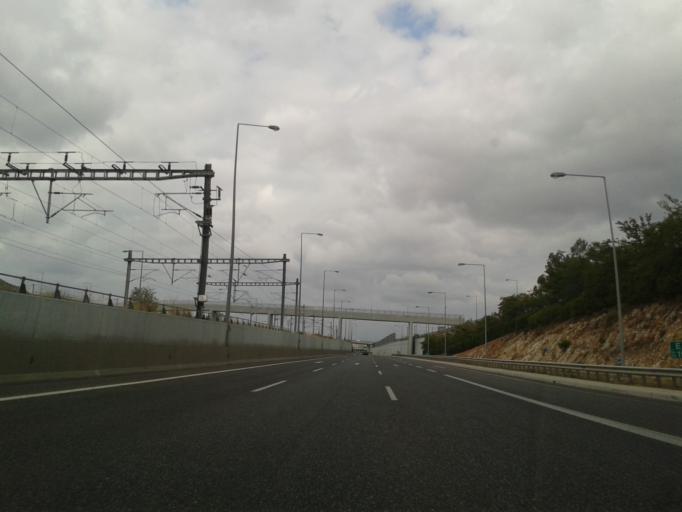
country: GR
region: Attica
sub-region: Nomarchia Dytikis Attikis
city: Zefyri
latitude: 38.0704
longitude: 23.7080
